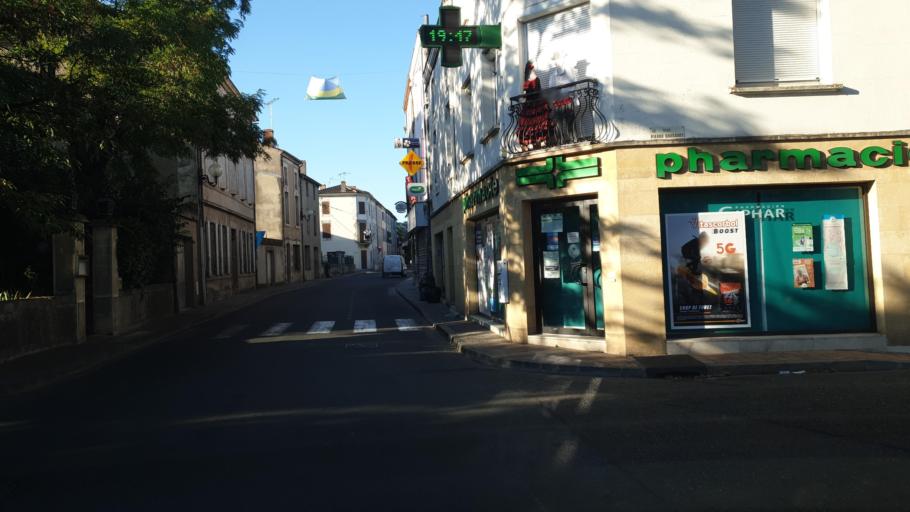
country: FR
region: Aquitaine
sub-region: Departement du Lot-et-Garonne
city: Castelmoron-sur-Lot
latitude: 44.3974
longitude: 0.4950
